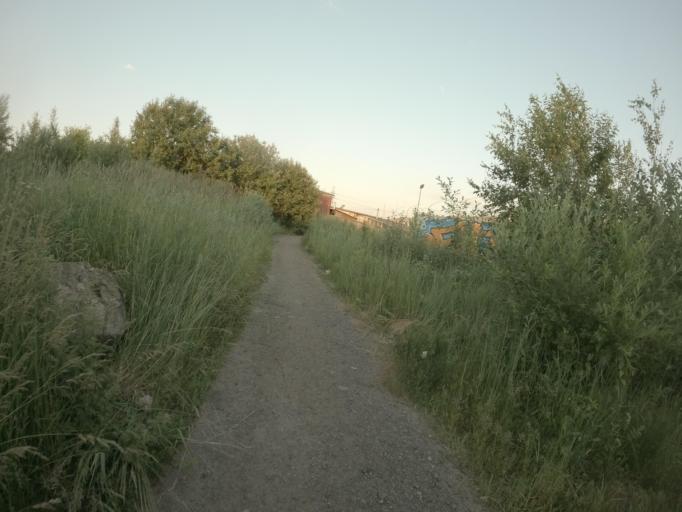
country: RU
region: St.-Petersburg
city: Avtovo
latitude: 59.8816
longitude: 30.2883
